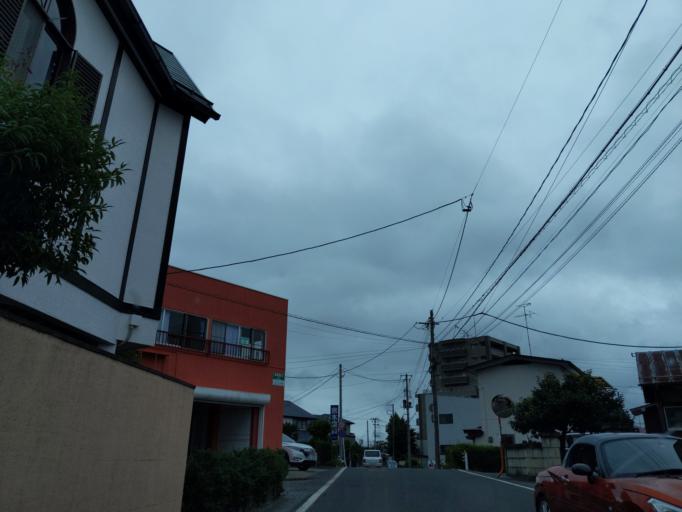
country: JP
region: Fukushima
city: Koriyama
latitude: 37.3904
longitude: 140.3533
